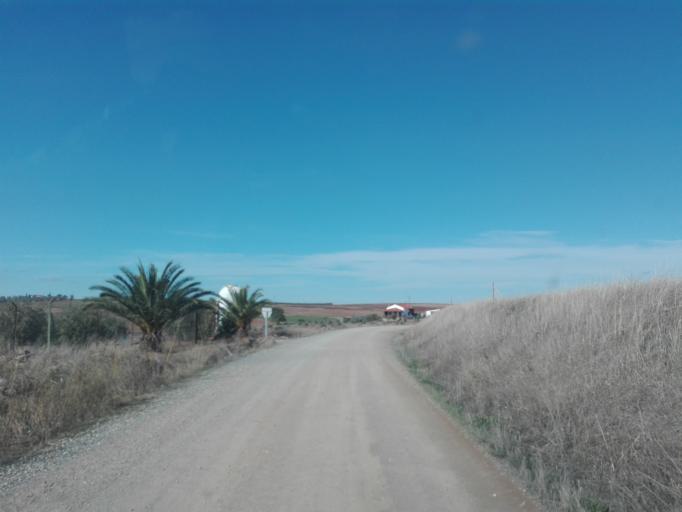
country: ES
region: Extremadura
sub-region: Provincia de Badajoz
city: Ahillones
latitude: 38.2606
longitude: -5.8721
